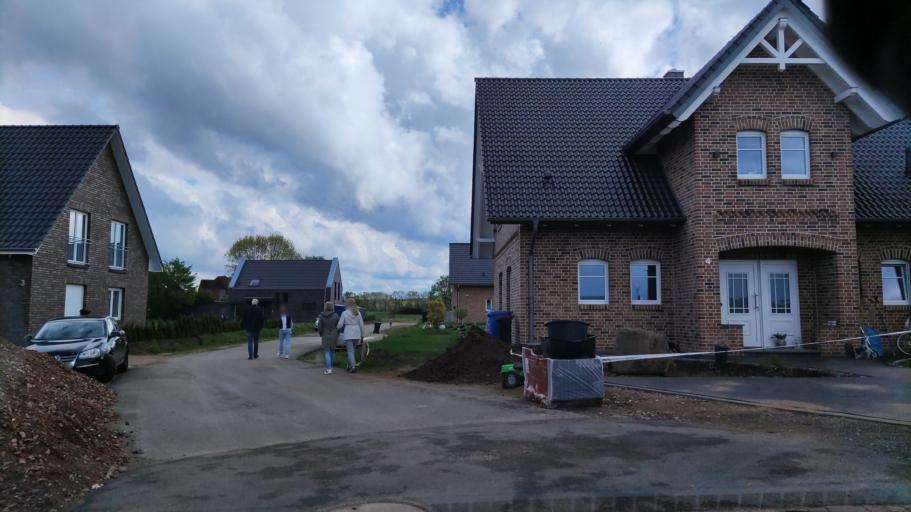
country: DE
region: Lower Saxony
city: Wulfsen
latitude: 53.3087
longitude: 10.1737
